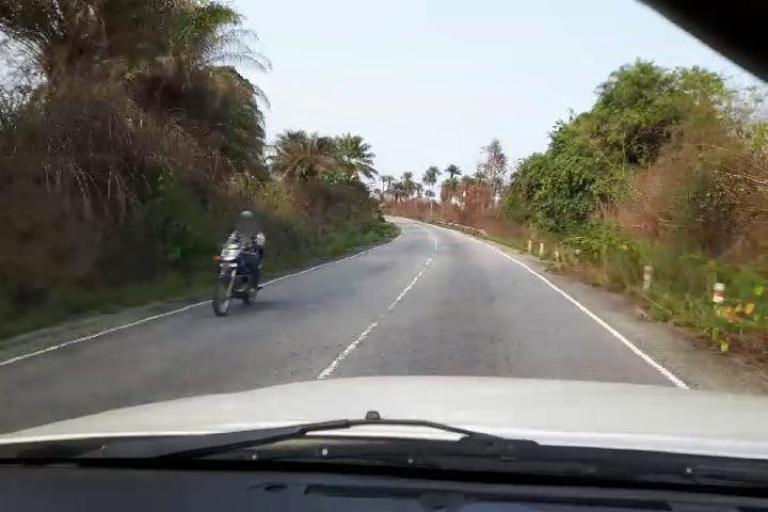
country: SL
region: Eastern Province
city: Blama
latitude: 7.9369
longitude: -11.5105
